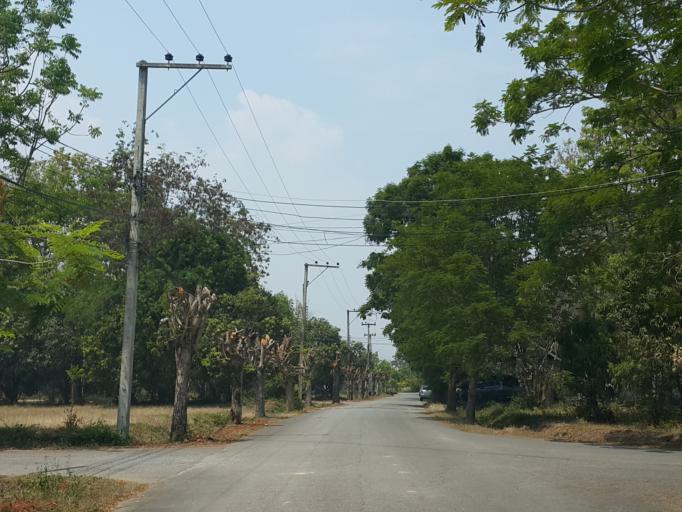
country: TH
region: Chiang Mai
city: Chiang Mai
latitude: 18.7315
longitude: 98.9741
